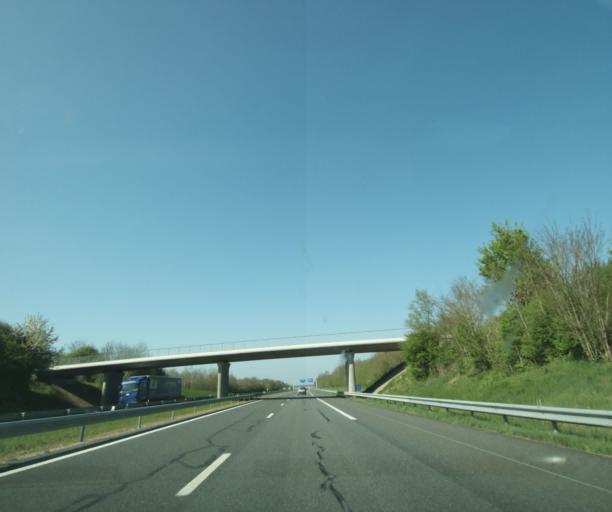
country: FR
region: Centre
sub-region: Departement du Loiret
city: Pannes
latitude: 48.0452
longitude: 2.6710
